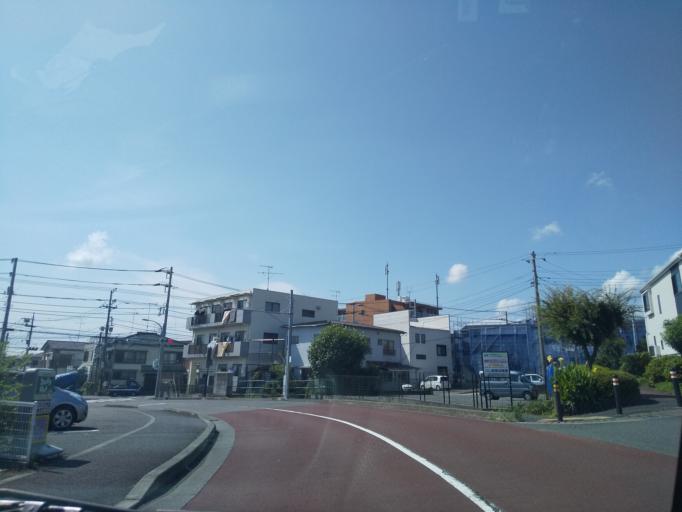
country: JP
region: Kanagawa
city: Zama
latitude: 35.4623
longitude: 139.4161
